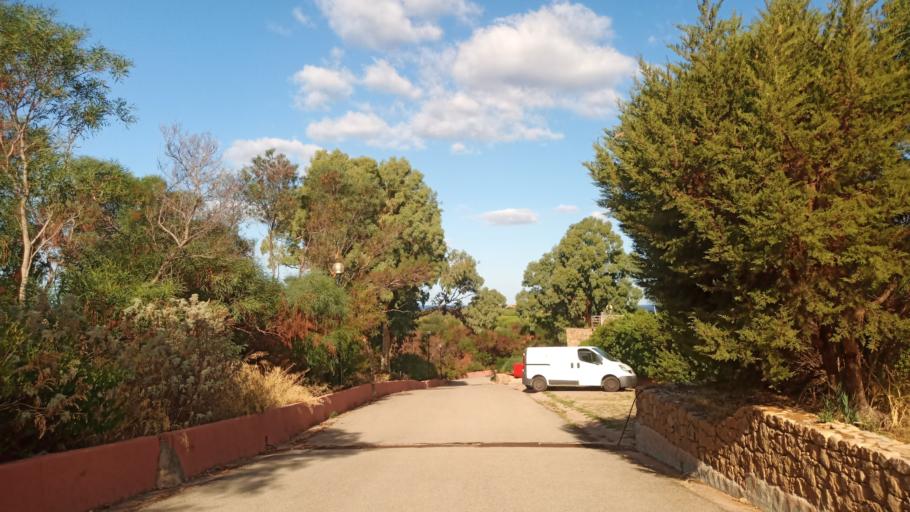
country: IT
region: Sardinia
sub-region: Provincia di Olbia-Tempio
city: Trinita d'Agultu
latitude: 41.0222
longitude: 8.8985
